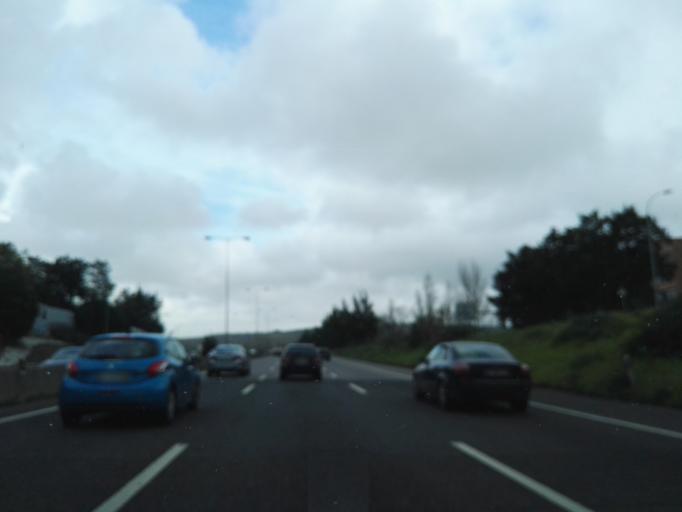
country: PT
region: Lisbon
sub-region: Amadora
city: Amadora
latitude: 38.7405
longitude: -9.2180
